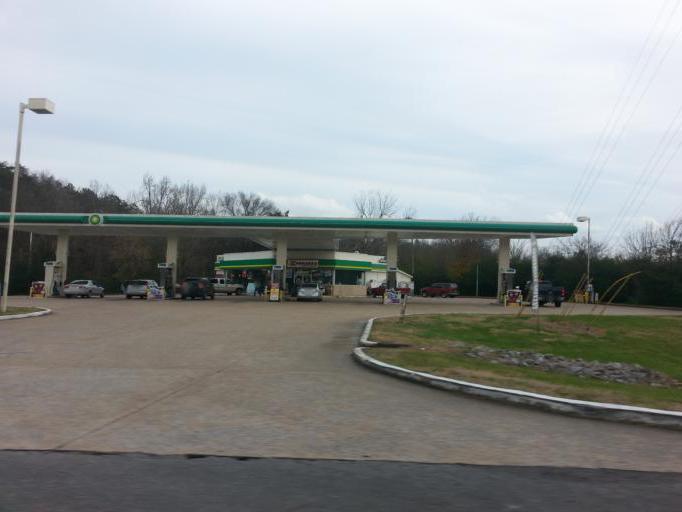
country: US
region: Tennessee
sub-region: Hamilton County
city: Sale Creek
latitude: 35.3404
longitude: -85.1291
